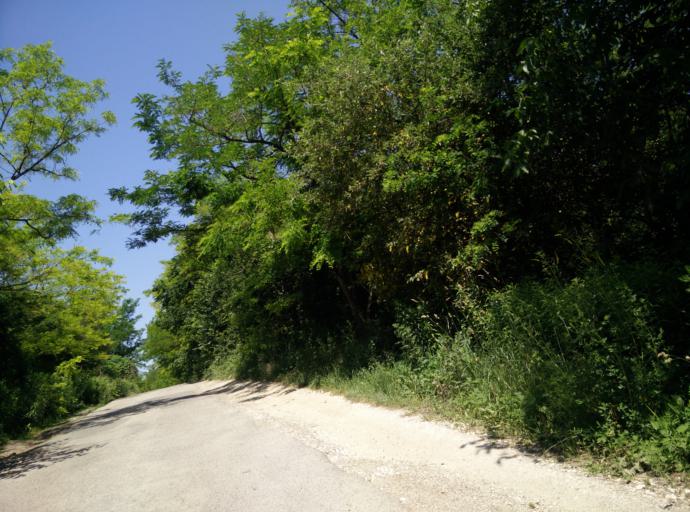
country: HU
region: Pest
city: Biatorbagy
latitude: 47.4588
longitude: 18.8232
